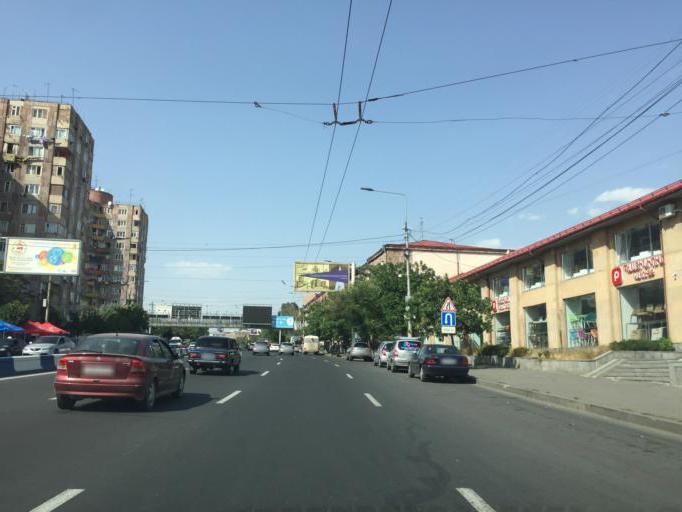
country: AM
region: Yerevan
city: Yerevan
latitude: 40.1553
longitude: 44.5008
